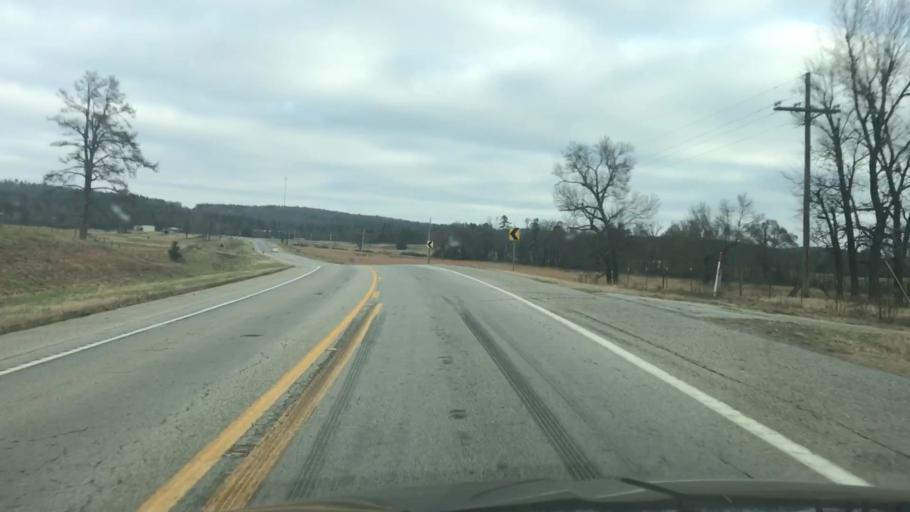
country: US
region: Arkansas
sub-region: Scott County
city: Waldron
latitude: 34.8011
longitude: -94.0418
